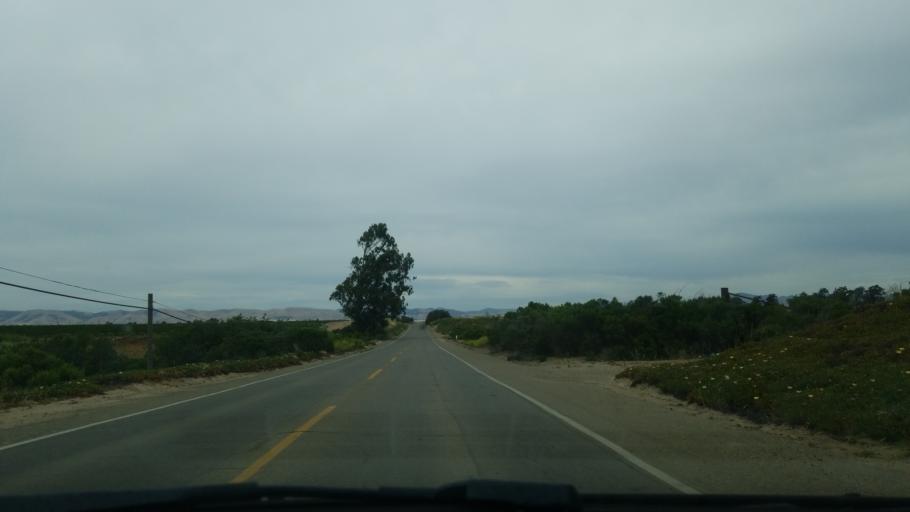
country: US
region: California
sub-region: Santa Barbara County
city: Santa Maria
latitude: 34.9124
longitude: -120.4860
